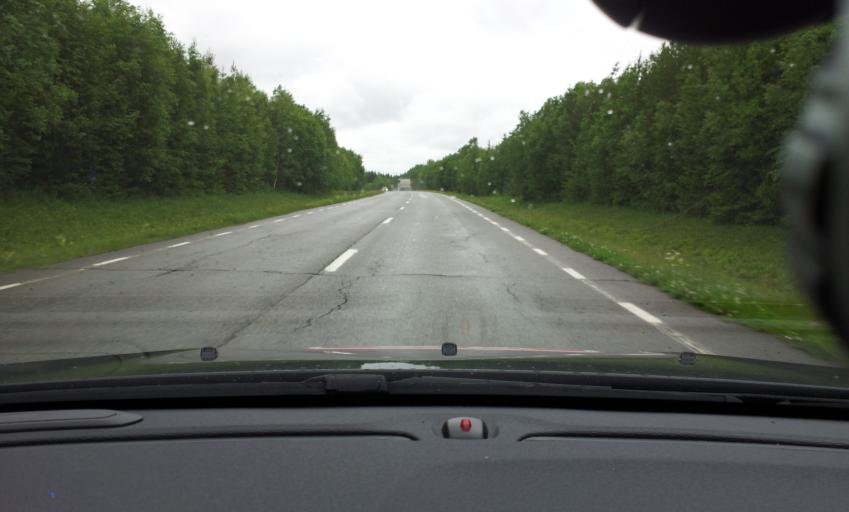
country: SE
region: Jaemtland
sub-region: OEstersunds Kommun
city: Lit
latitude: 63.6168
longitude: 14.6752
